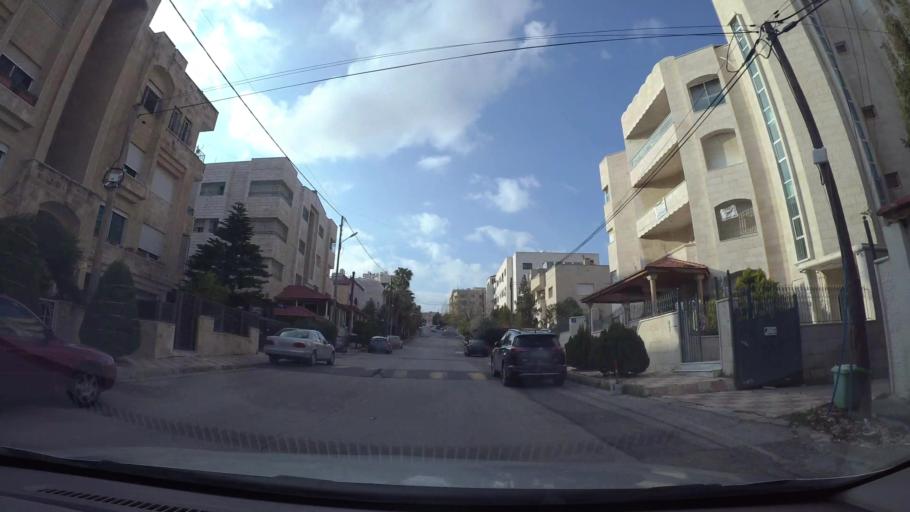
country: JO
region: Amman
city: Al Jubayhah
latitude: 31.9821
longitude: 35.8571
